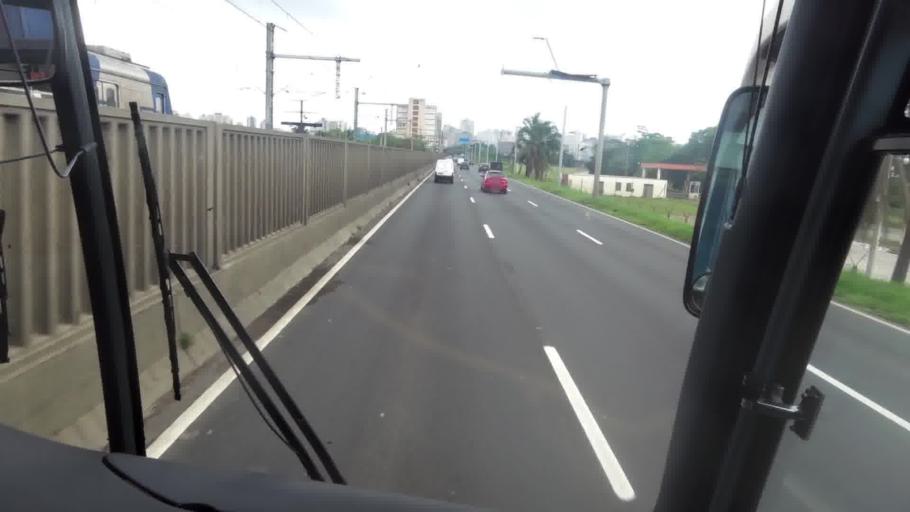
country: BR
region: Rio Grande do Sul
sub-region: Porto Alegre
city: Porto Alegre
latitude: -30.0171
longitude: -51.2151
